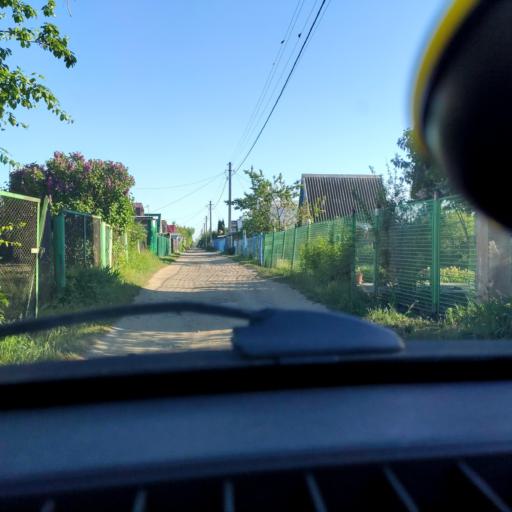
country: RU
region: Samara
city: Tol'yatti
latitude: 53.5974
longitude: 49.3162
